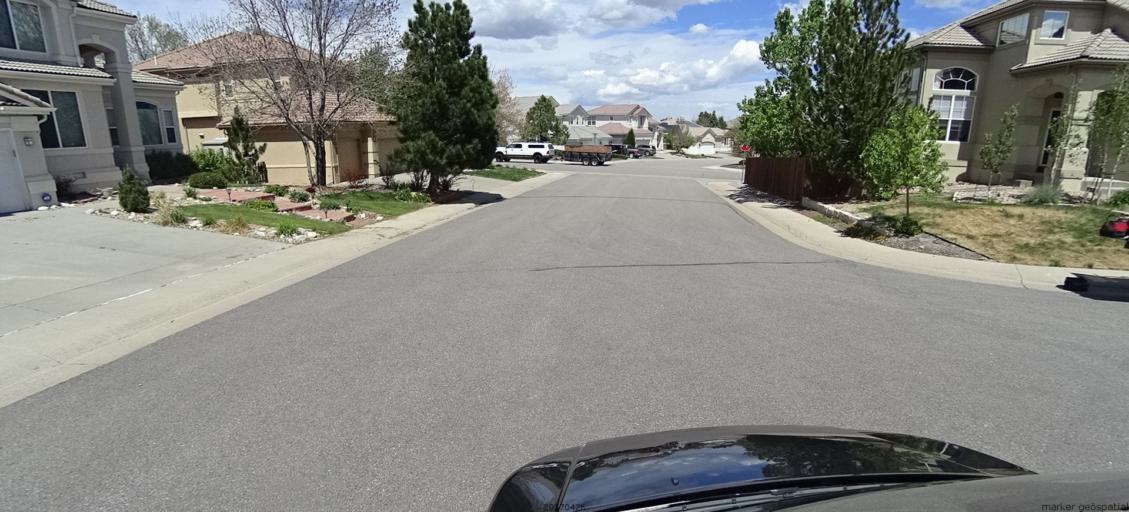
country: US
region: Colorado
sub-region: Douglas County
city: Carriage Club
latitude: 39.5399
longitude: -104.8912
